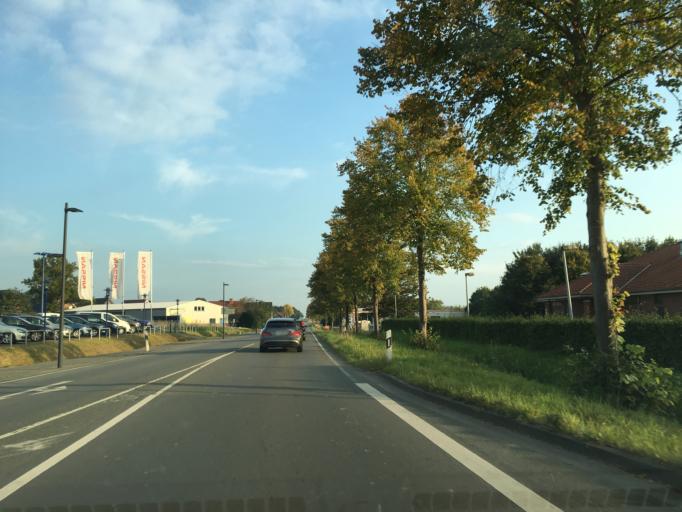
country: DE
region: North Rhine-Westphalia
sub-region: Regierungsbezirk Munster
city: Altenberge
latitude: 52.0411
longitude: 7.4697
